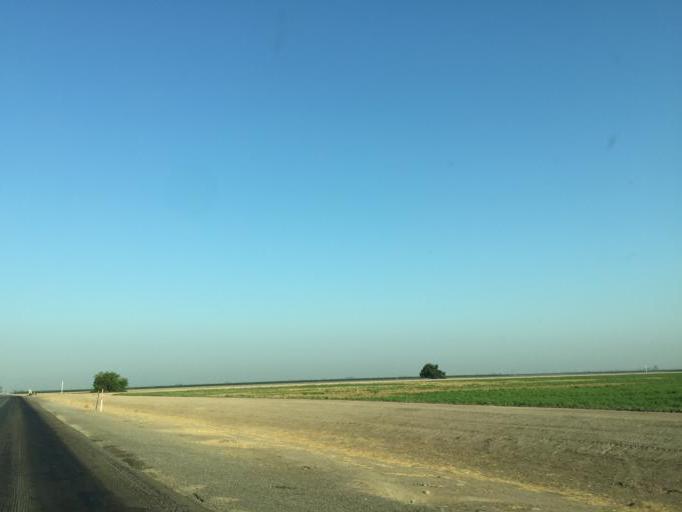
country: US
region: California
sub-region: Tulare County
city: Cutler
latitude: 36.4581
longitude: -119.3466
